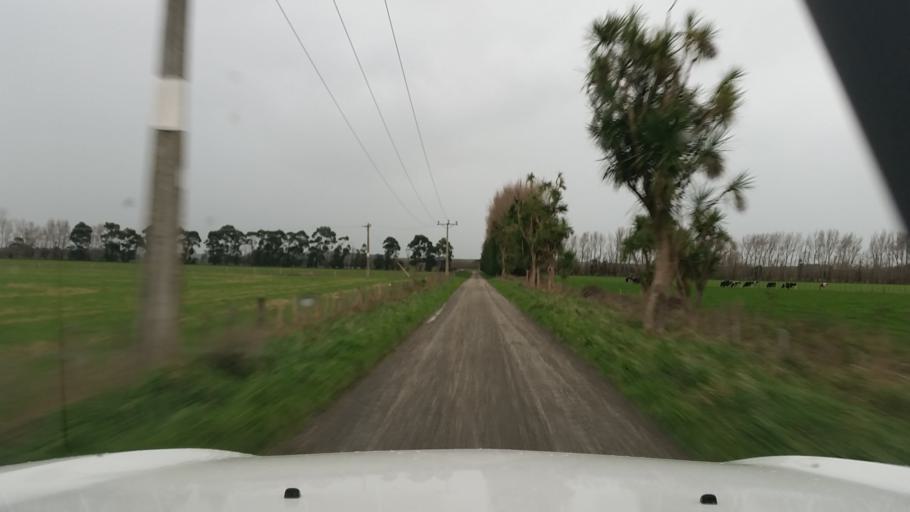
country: NZ
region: Wellington
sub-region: South Wairarapa District
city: Waipawa
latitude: -41.2295
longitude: 175.4014
